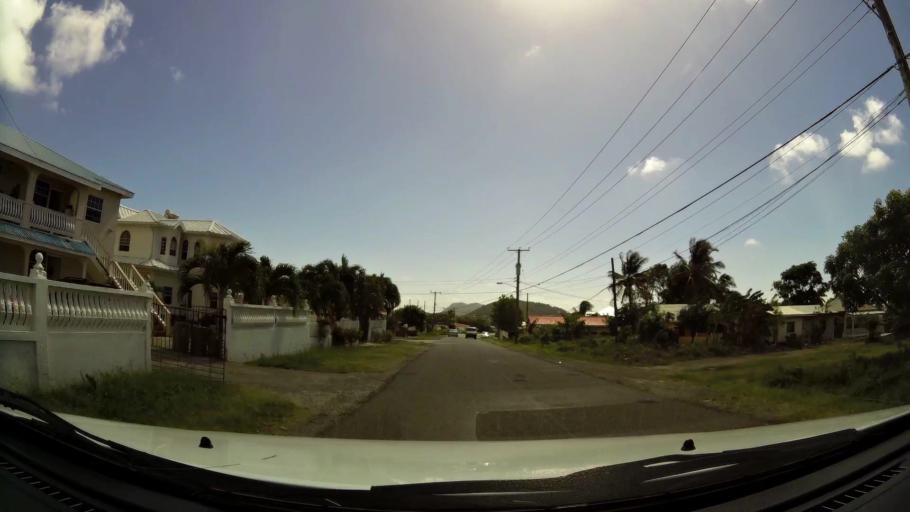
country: LC
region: Laborie Quarter
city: Laborie
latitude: 13.7581
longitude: -60.9732
